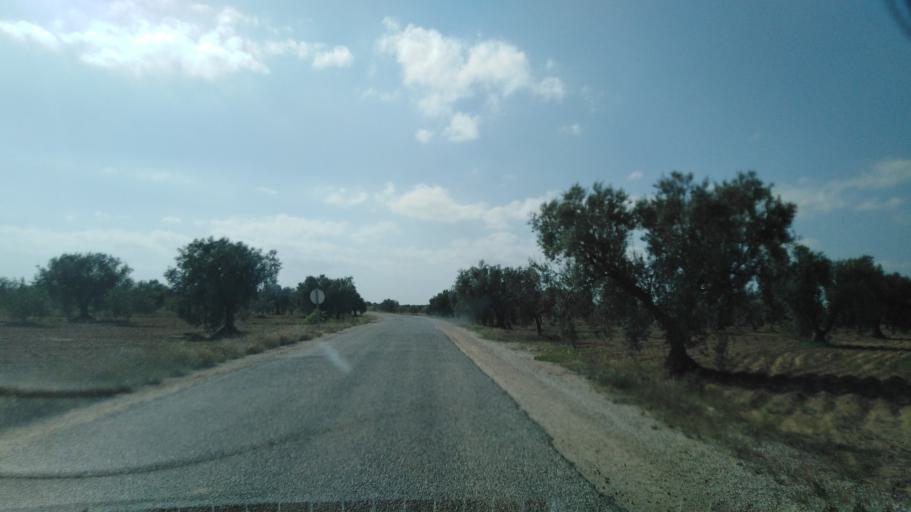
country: TN
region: Safaqis
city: Bi'r `Ali Bin Khalifah
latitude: 34.7770
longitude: 10.3616
